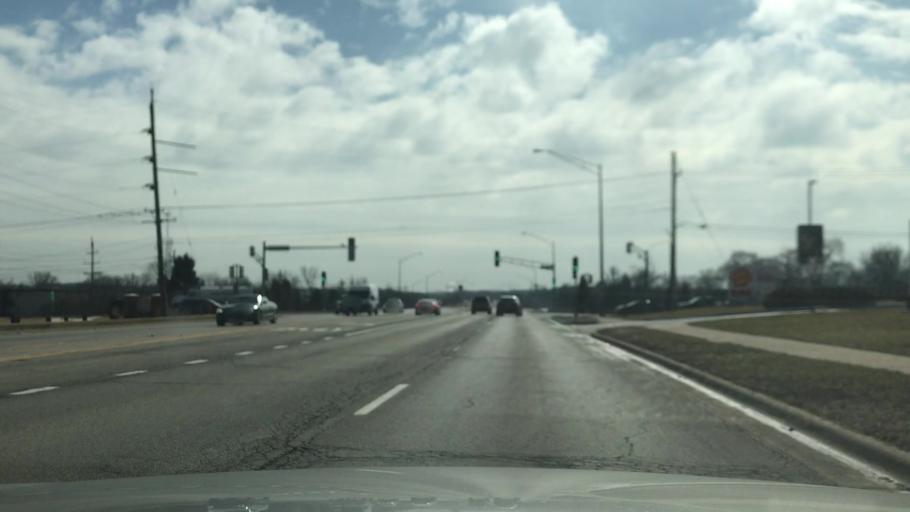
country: US
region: Illinois
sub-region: DuPage County
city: Darien
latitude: 41.7377
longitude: -87.9735
